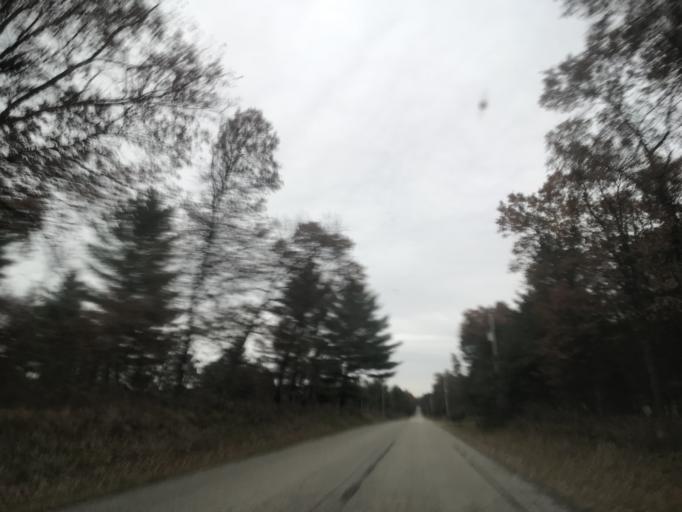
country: US
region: Wisconsin
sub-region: Oconto County
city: Gillett
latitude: 45.3075
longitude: -88.2694
